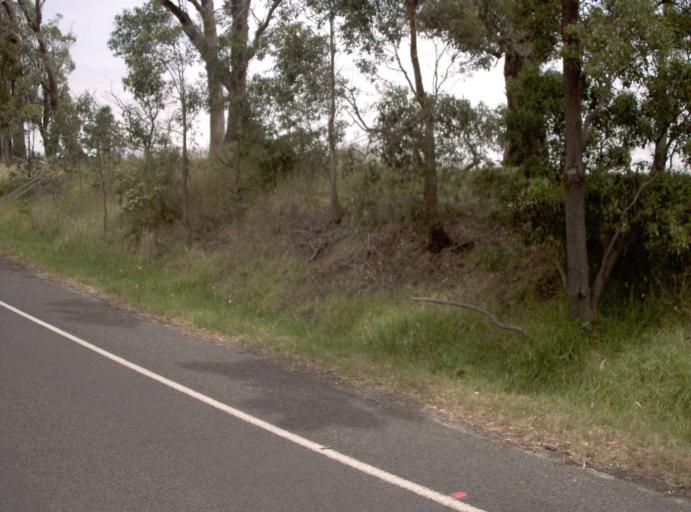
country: AU
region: Victoria
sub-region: Latrobe
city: Traralgon
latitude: -38.4739
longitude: 146.7169
